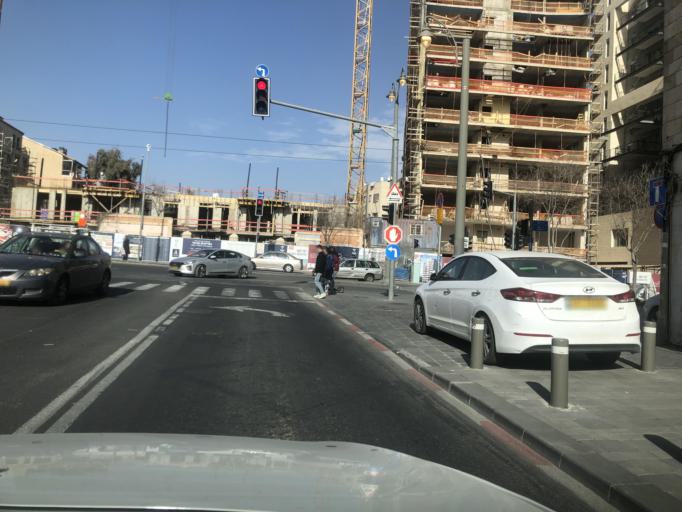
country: IL
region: Jerusalem
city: West Jerusalem
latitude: 31.7865
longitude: 35.2090
